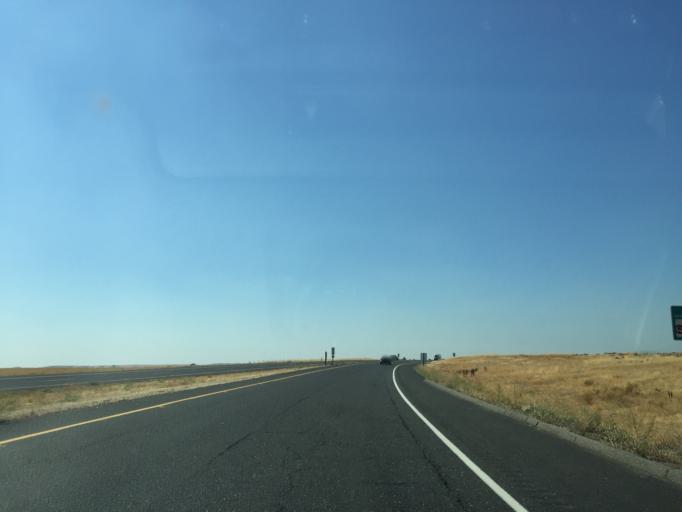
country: US
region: California
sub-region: Calaveras County
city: Copperopolis
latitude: 37.8236
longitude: -120.6400
